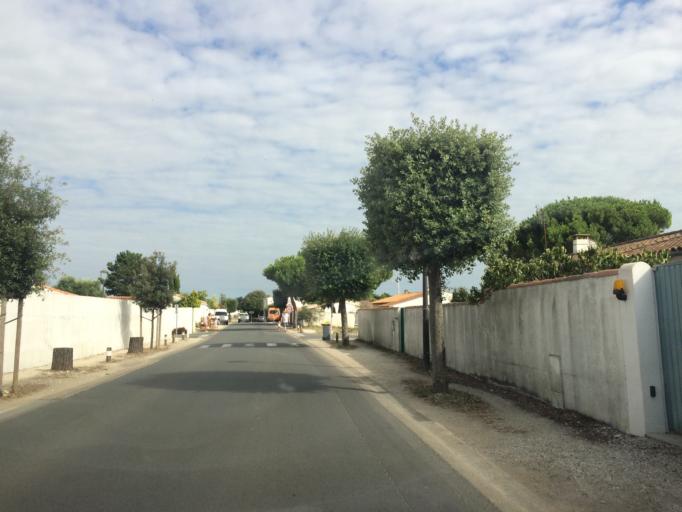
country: FR
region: Poitou-Charentes
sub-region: Departement de la Charente-Maritime
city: La Flotte
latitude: 46.1854
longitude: -1.3319
